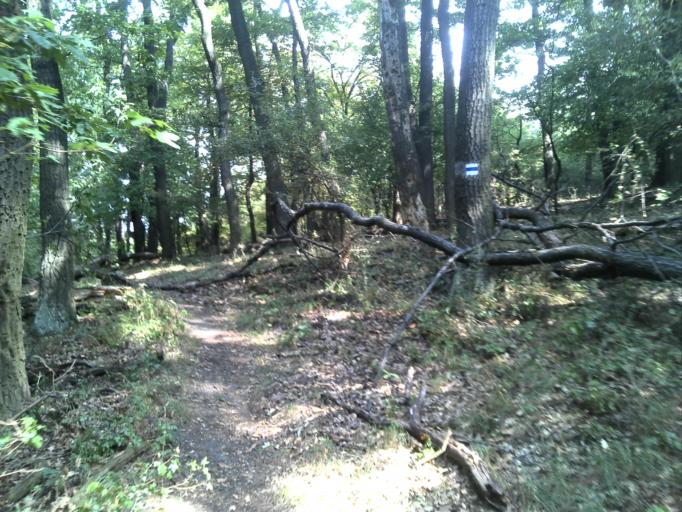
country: HU
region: Komarom-Esztergom
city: Oroszlany
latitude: 47.4308
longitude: 18.3441
